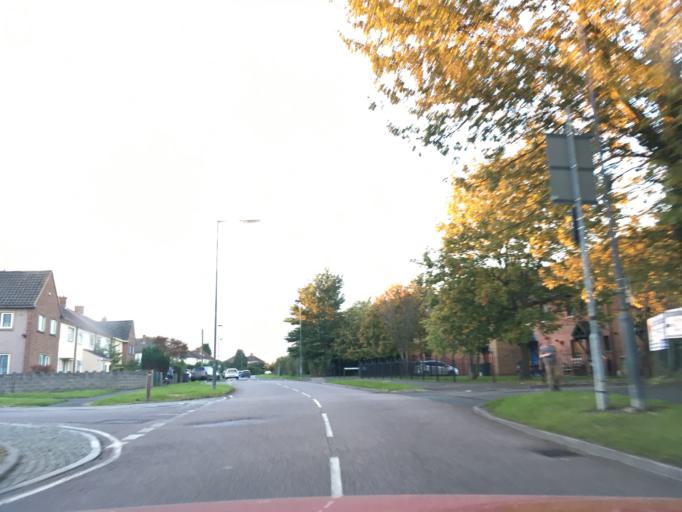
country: GB
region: England
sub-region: South Gloucestershire
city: Stoke Gifford
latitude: 51.5256
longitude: -2.5546
